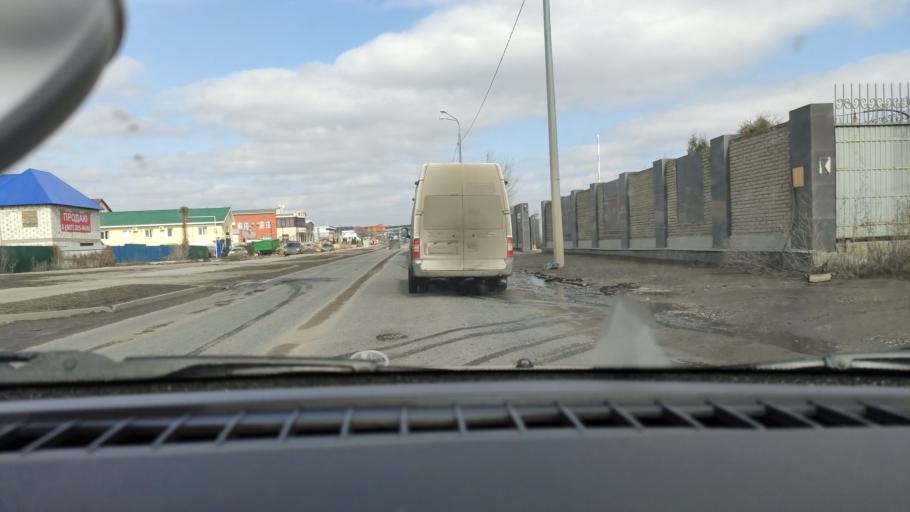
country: RU
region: Samara
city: Petra-Dubrava
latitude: 53.2665
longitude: 50.2592
